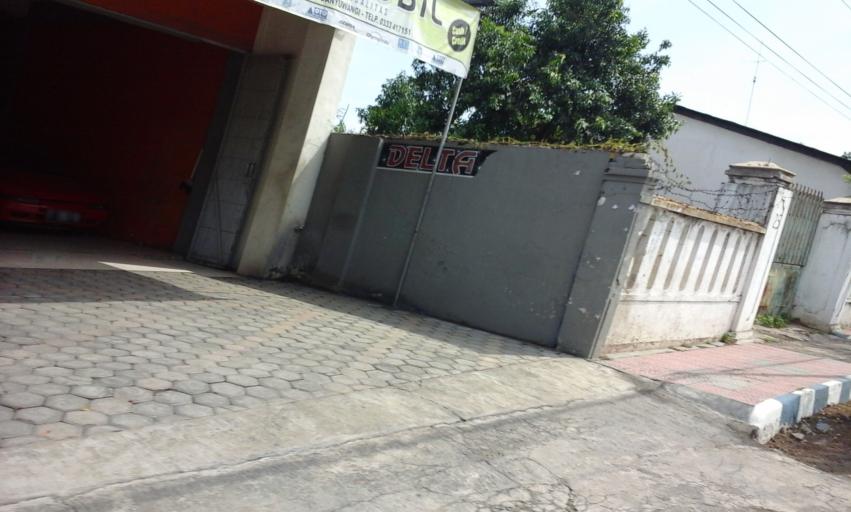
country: ID
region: East Java
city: Krajan
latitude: -8.2442
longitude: 114.3519
